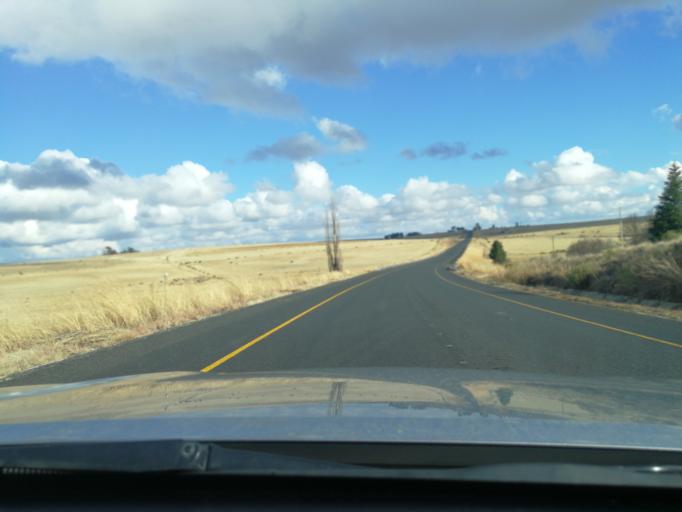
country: ZA
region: Orange Free State
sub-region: Thabo Mofutsanyana District Municipality
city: Reitz
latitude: -27.9048
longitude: 28.3961
